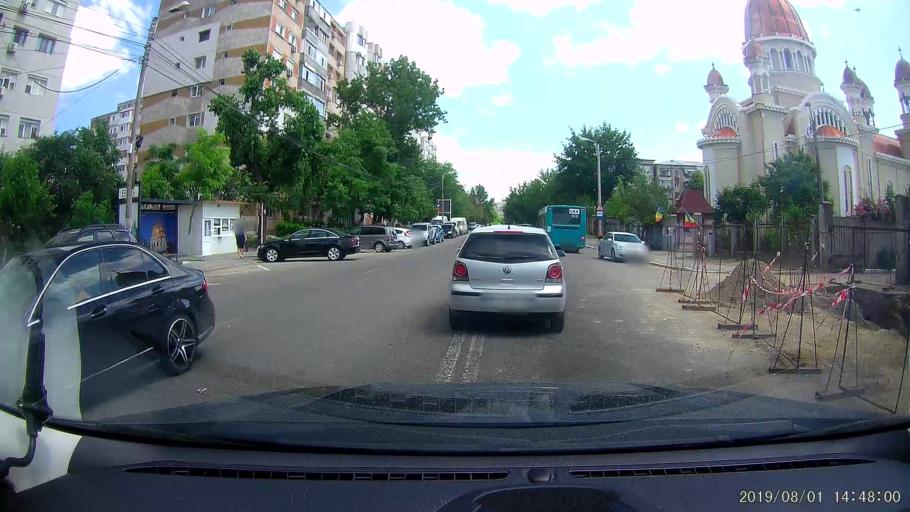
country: RO
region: Galati
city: Galati
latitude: 45.4130
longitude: 28.0064
